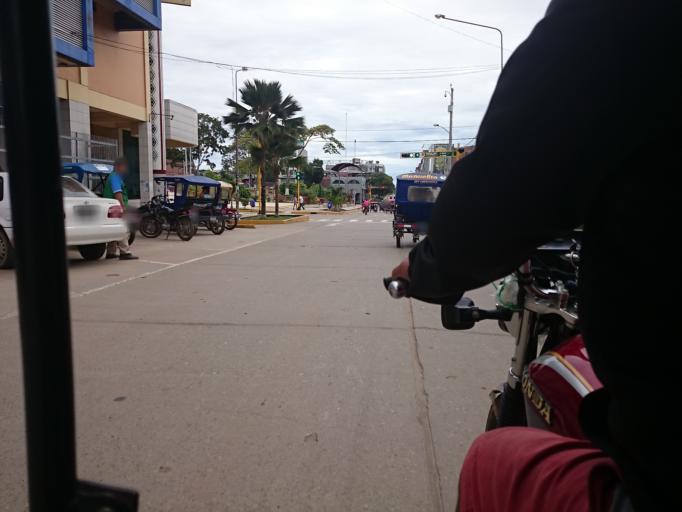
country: PE
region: Ucayali
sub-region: Provincia de Coronel Portillo
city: Pucallpa
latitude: -8.3843
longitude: -74.5324
